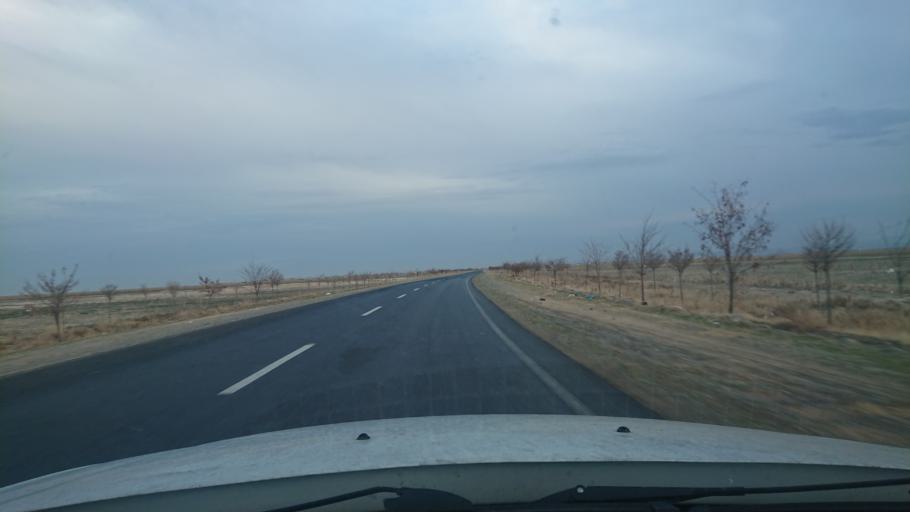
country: TR
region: Aksaray
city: Yesilova
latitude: 38.3109
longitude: 33.7539
